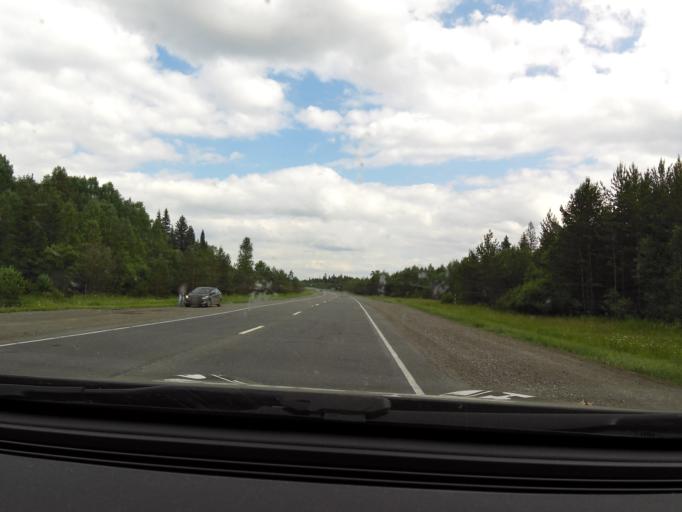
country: RU
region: Sverdlovsk
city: Atig
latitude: 56.7974
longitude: 59.3941
